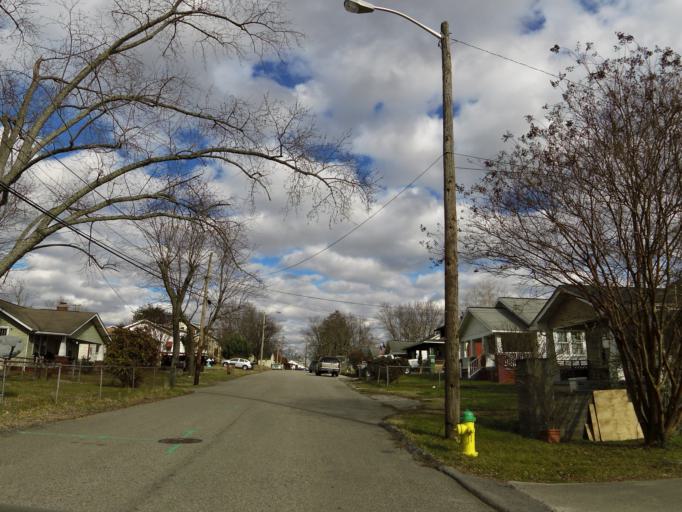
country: US
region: Tennessee
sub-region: Knox County
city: Knoxville
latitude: 35.9981
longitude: -83.9402
